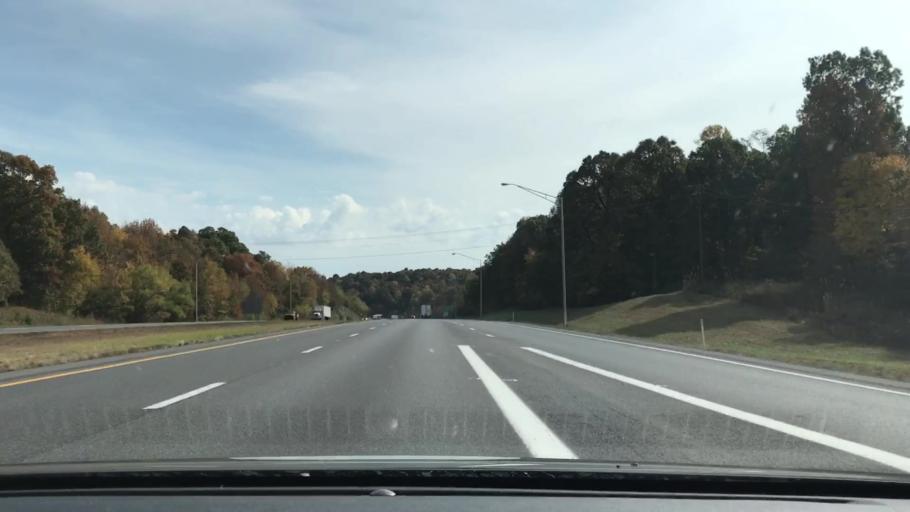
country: US
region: Kentucky
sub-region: Lyon County
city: Eddyville
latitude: 37.0728
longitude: -88.1175
